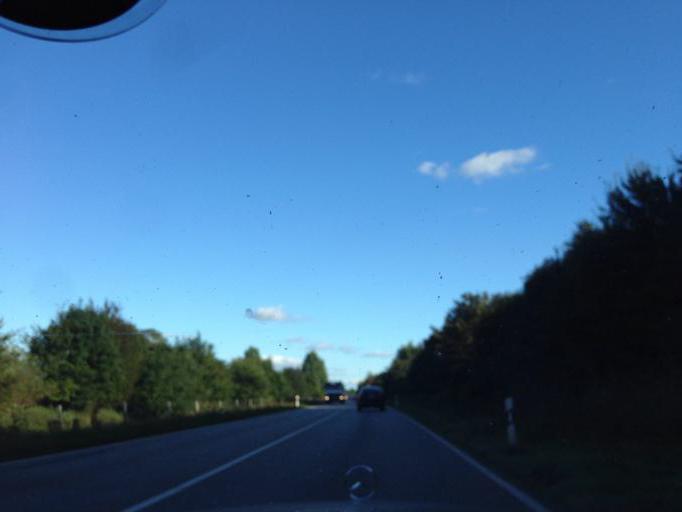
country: DE
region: Schleswig-Holstein
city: Boostedt
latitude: 54.0271
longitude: 10.0495
